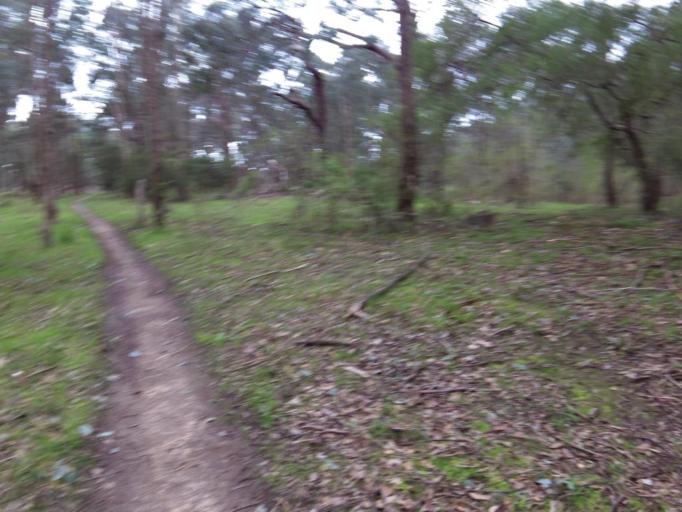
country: AU
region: Victoria
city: Plenty
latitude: -37.6745
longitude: 145.1041
